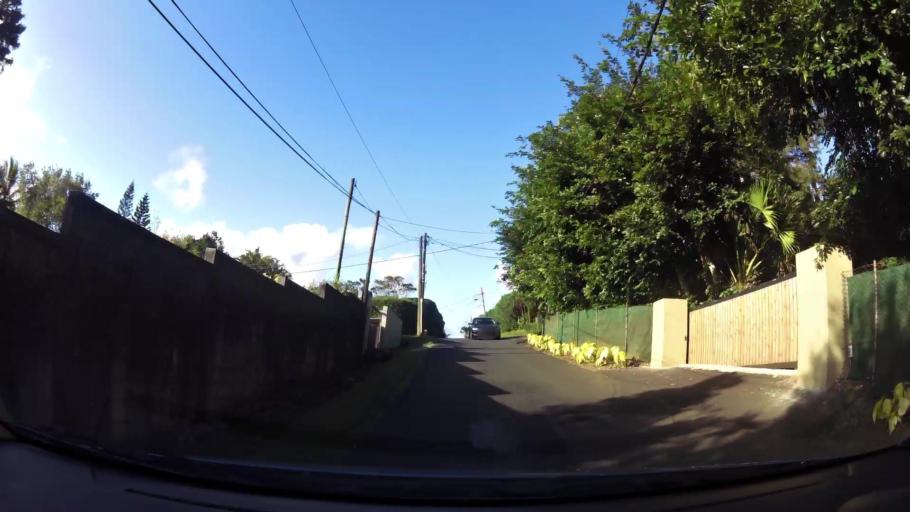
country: MU
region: Plaines Wilhems
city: Curepipe
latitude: -20.3169
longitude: 57.5086
